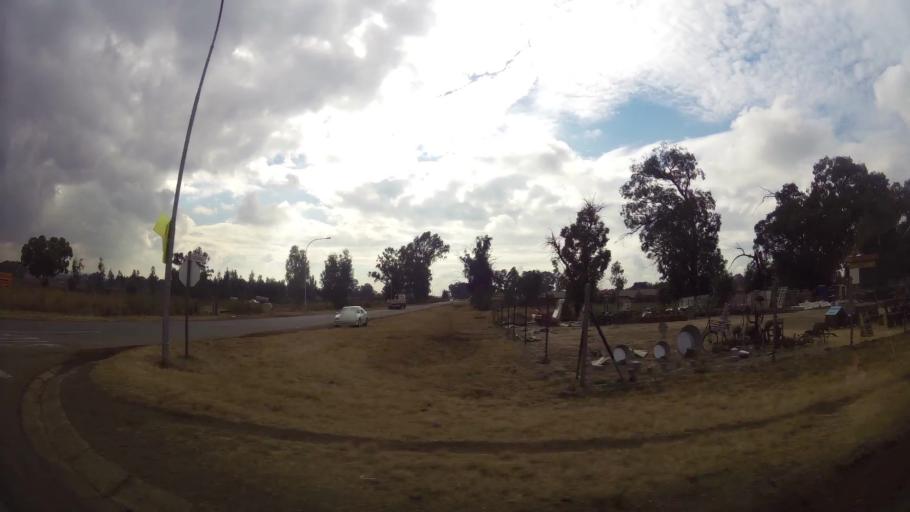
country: ZA
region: Gauteng
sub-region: Sedibeng District Municipality
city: Meyerton
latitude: -26.5888
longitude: 28.0228
